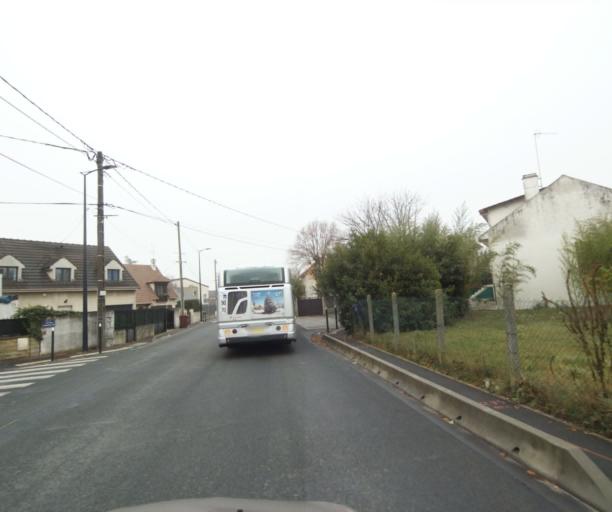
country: FR
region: Ile-de-France
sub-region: Departement de Seine-Saint-Denis
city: Coubron
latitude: 48.9085
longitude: 2.5856
